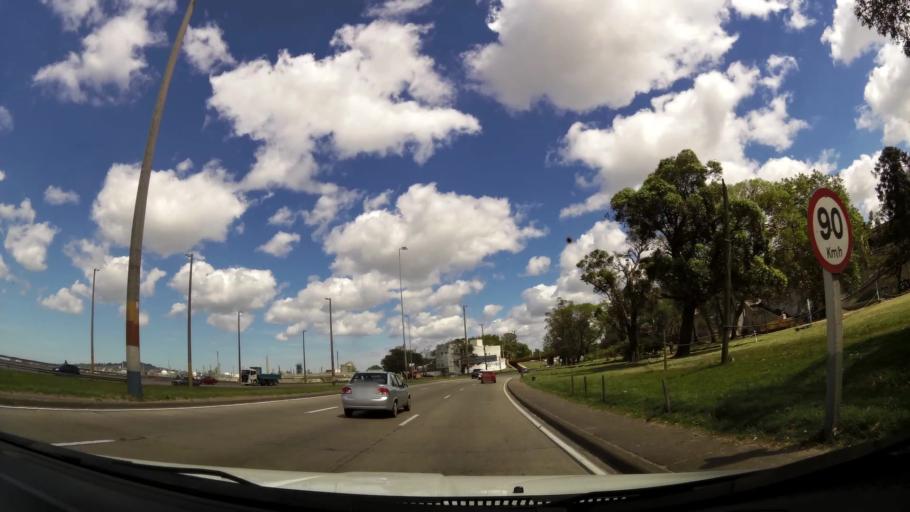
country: UY
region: Montevideo
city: Montevideo
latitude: -34.8743
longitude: -56.2146
